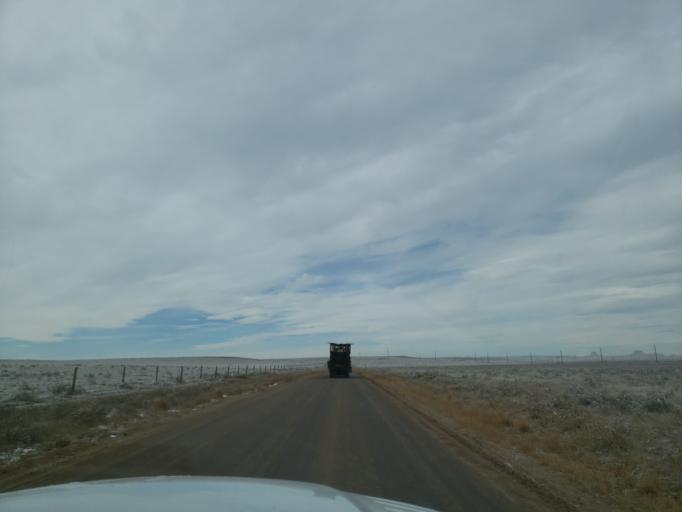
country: US
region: Wyoming
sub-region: Laramie County
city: Pine Bluffs
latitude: 40.7877
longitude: -103.8814
